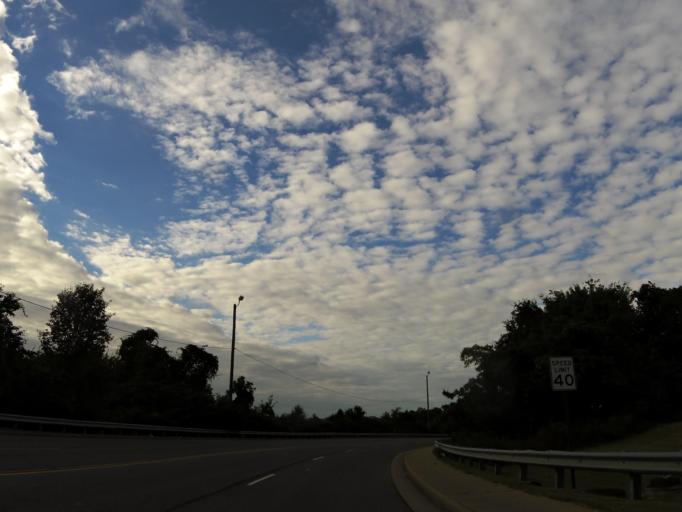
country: US
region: Tennessee
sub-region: Davidson County
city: Nashville
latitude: 36.1676
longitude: -86.8350
